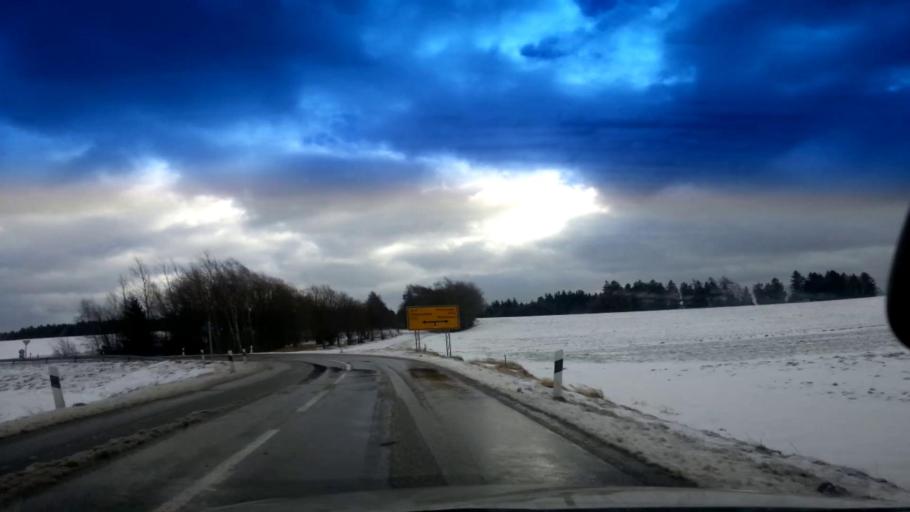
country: DE
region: Bavaria
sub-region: Upper Franconia
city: Kirchenlamitz
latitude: 50.1479
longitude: 11.9578
